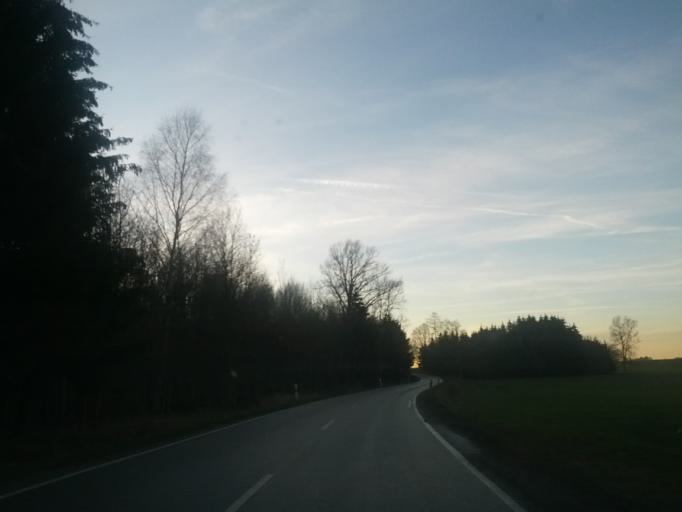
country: DE
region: Baden-Wuerttemberg
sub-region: Tuebingen Region
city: Berkheim
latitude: 48.0269
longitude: 10.0669
